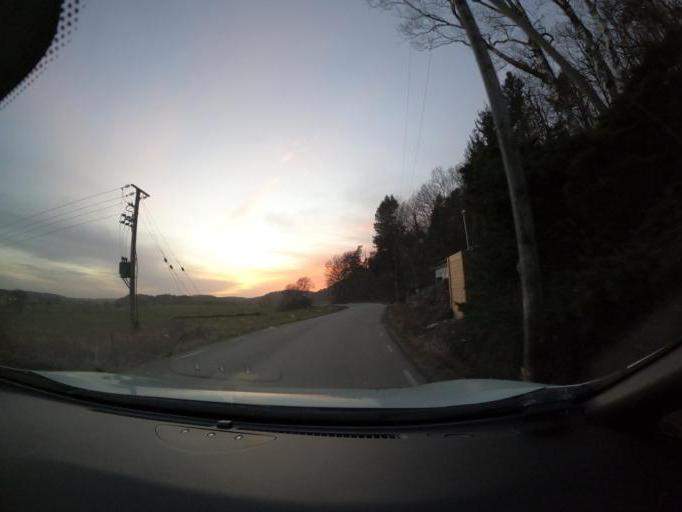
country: SE
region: Vaestra Goetaland
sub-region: Harryda Kommun
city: Molnlycke
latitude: 57.6051
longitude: 12.1620
